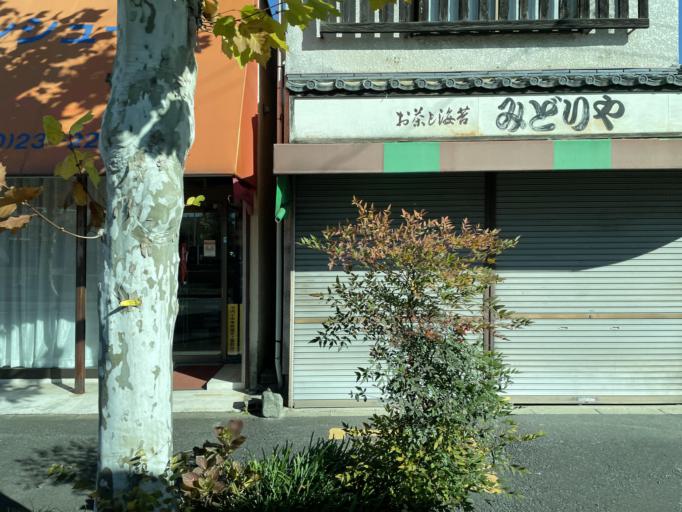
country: JP
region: Saitama
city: Kukichuo
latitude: 36.0698
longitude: 139.6970
